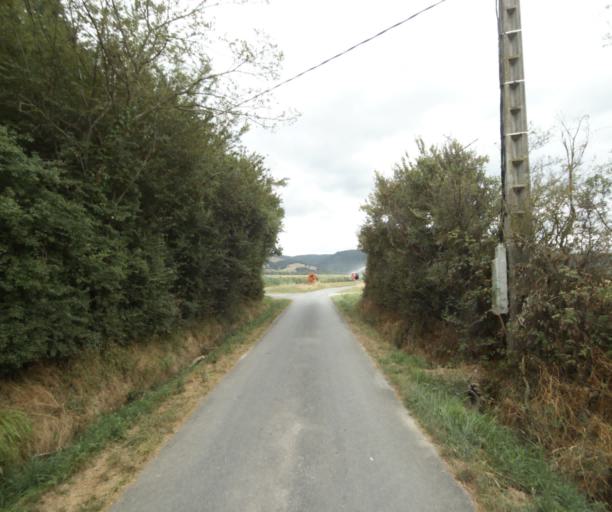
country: FR
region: Midi-Pyrenees
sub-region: Departement du Tarn
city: Soreze
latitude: 43.4726
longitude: 2.0664
